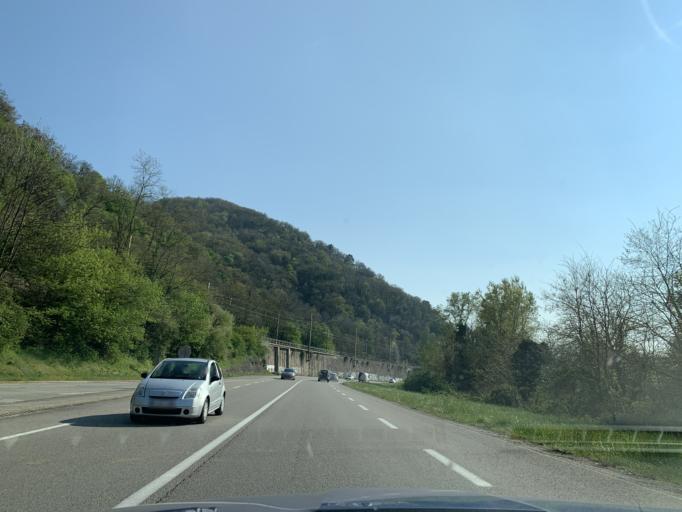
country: FR
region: Rhone-Alpes
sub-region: Departement de la Drome
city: Saint-Vallier
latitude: 45.1478
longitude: 4.8276
